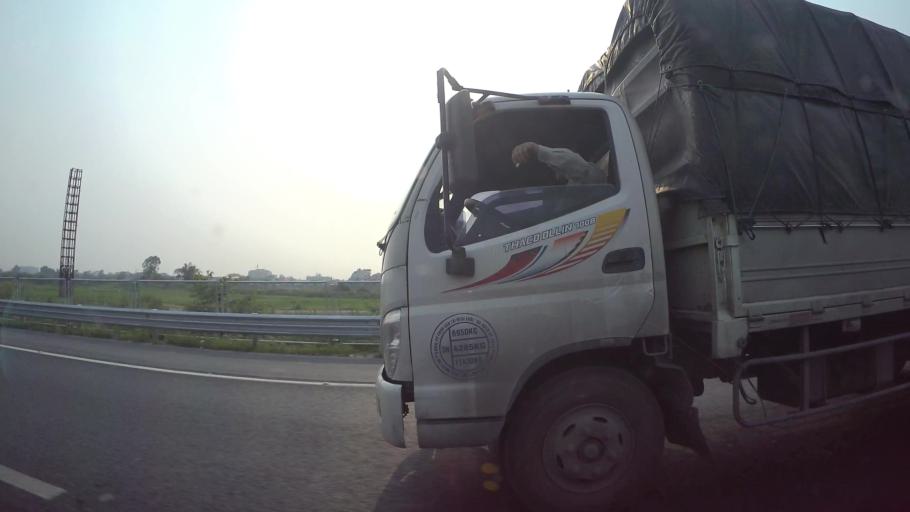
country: VN
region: Ha Noi
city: Van Dien
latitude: 20.9209
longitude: 105.8598
